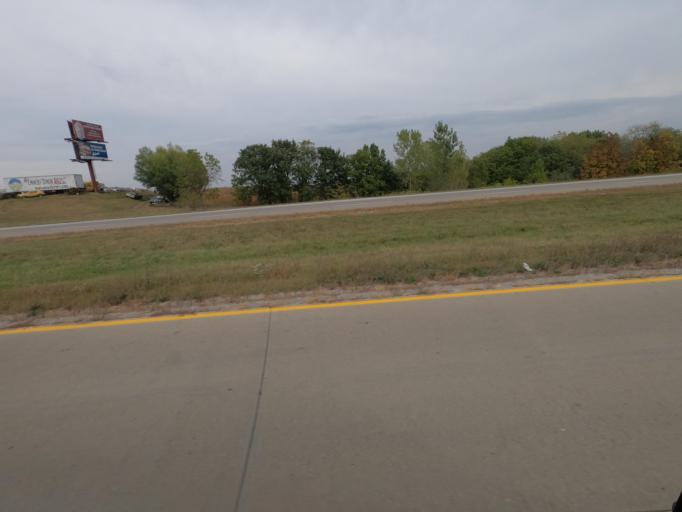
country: US
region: Iowa
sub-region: Marion County
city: Pella
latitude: 41.3874
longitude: -92.8291
